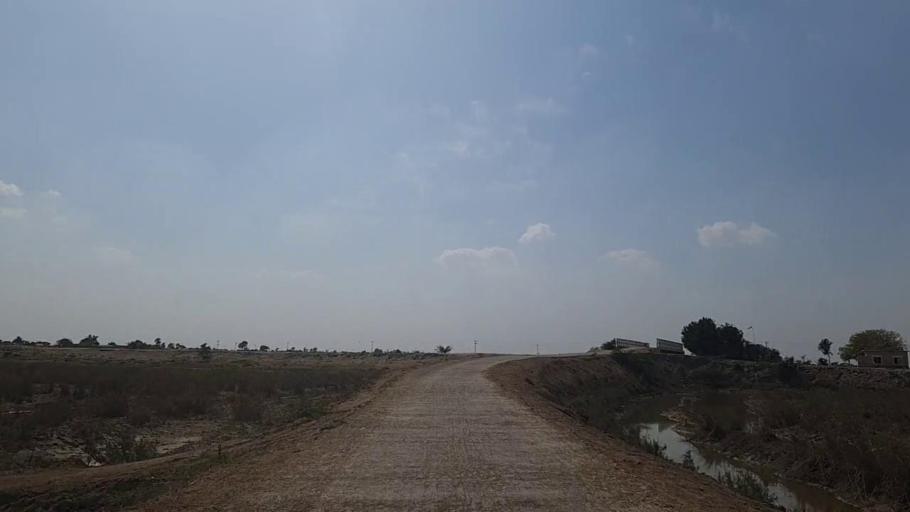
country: PK
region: Sindh
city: Jati
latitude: 24.4786
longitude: 68.2699
